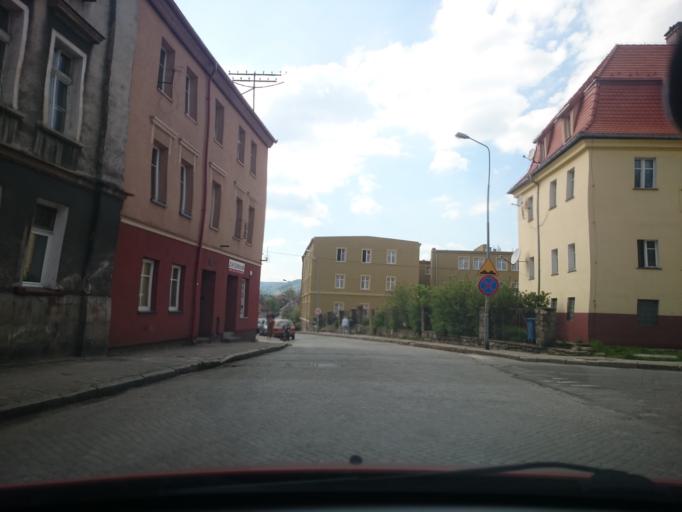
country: PL
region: Lower Silesian Voivodeship
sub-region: Powiat klodzki
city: Bystrzyca Klodzka
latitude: 50.2987
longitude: 16.6478
